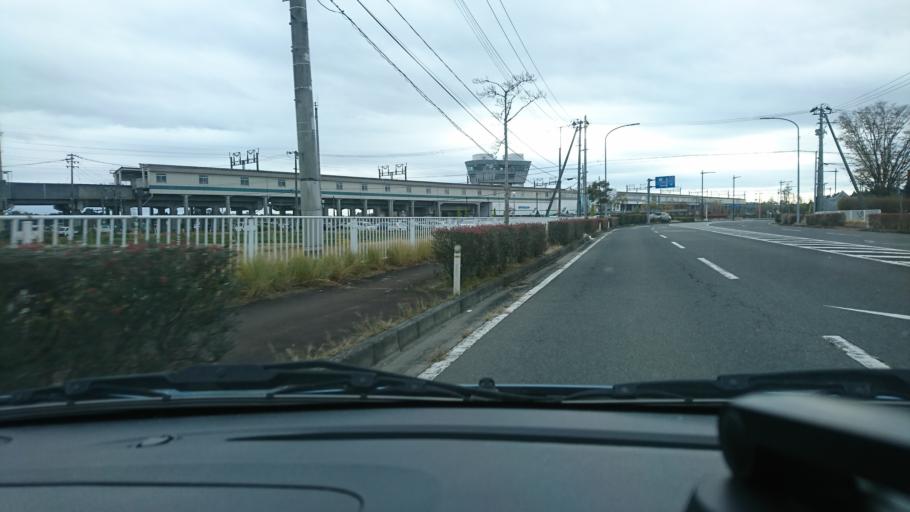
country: JP
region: Iwate
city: Ichinoseki
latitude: 38.7513
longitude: 141.0715
